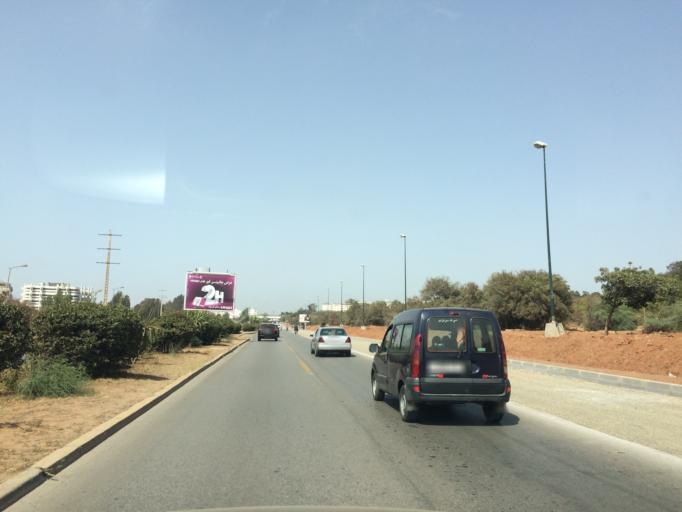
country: MA
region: Rabat-Sale-Zemmour-Zaer
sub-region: Rabat
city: Rabat
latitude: 33.9806
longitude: -6.8577
